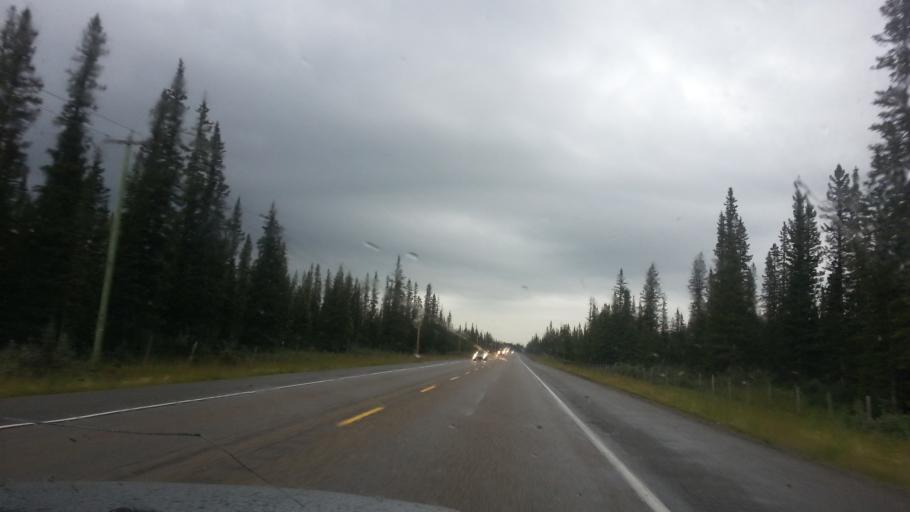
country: CA
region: Alberta
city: Cochrane
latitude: 50.9629
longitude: -114.5475
